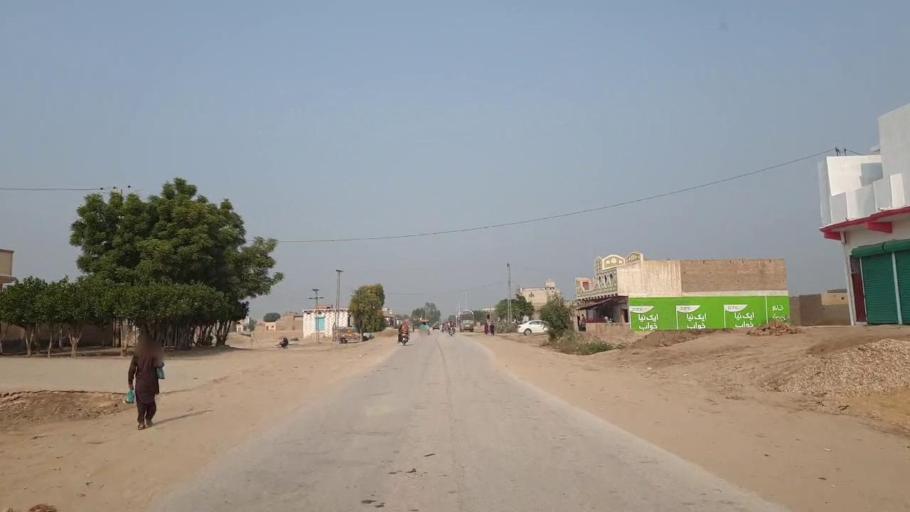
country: PK
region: Sindh
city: Bhan
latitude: 26.5646
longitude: 67.7237
